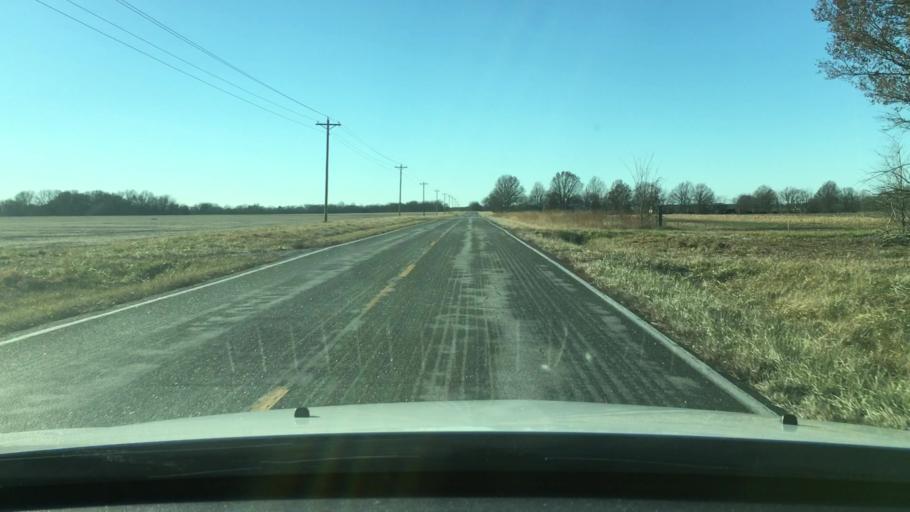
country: US
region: Missouri
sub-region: Audrain County
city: Mexico
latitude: 39.2809
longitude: -91.7487
